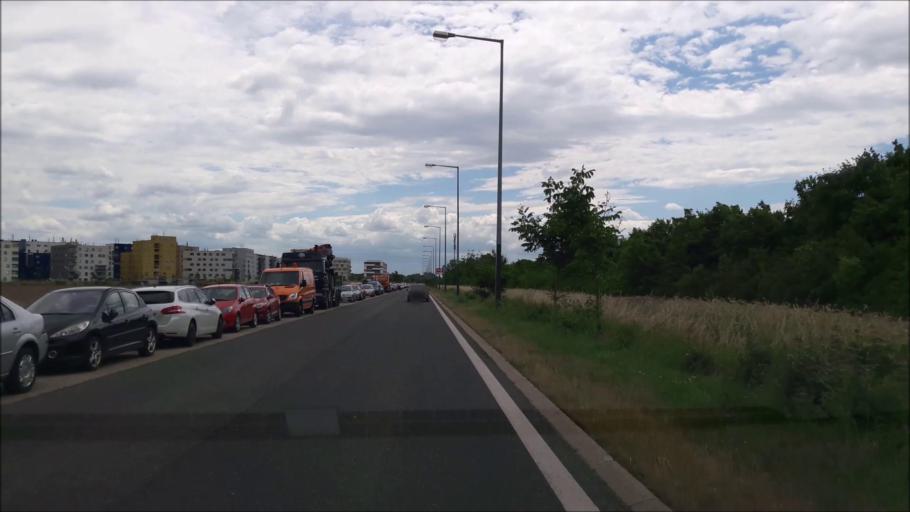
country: AT
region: Lower Austria
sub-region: Politischer Bezirk Ganserndorf
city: Gross-Enzersdorf
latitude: 48.2300
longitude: 16.4984
